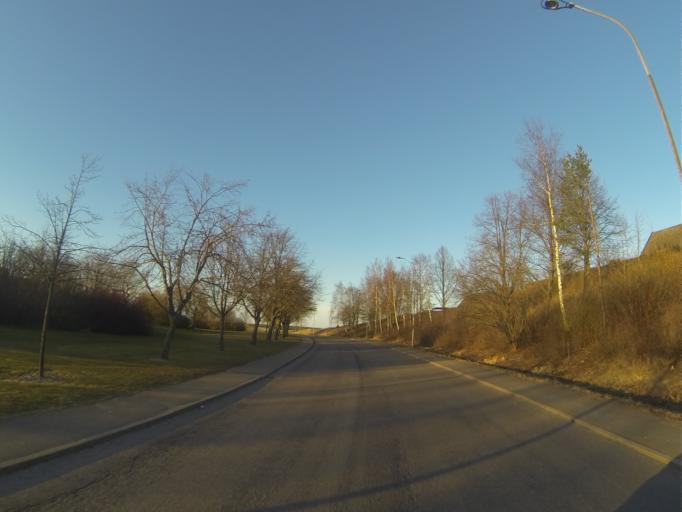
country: SE
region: Skane
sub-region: Staffanstorps Kommun
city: Staffanstorp
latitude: 55.5866
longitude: 13.1833
